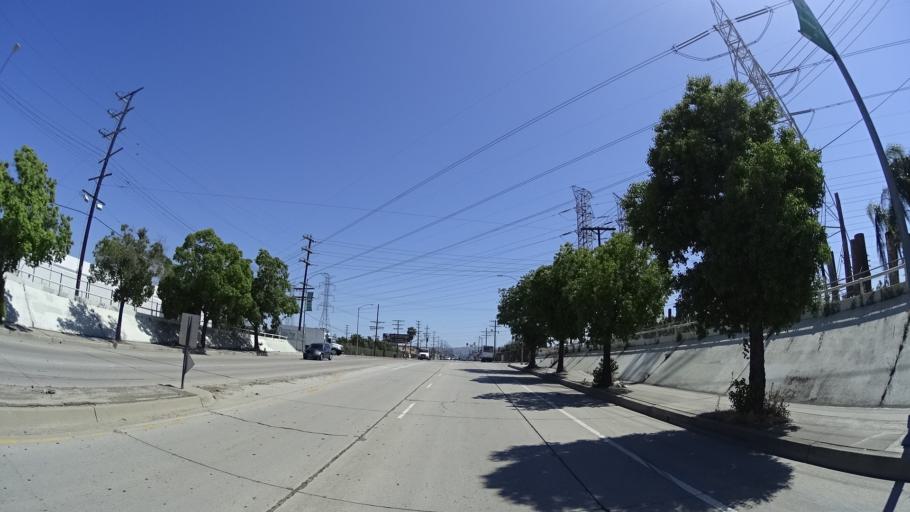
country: US
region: California
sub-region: Los Angeles County
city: North Hollywood
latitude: 34.1991
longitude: -118.3879
